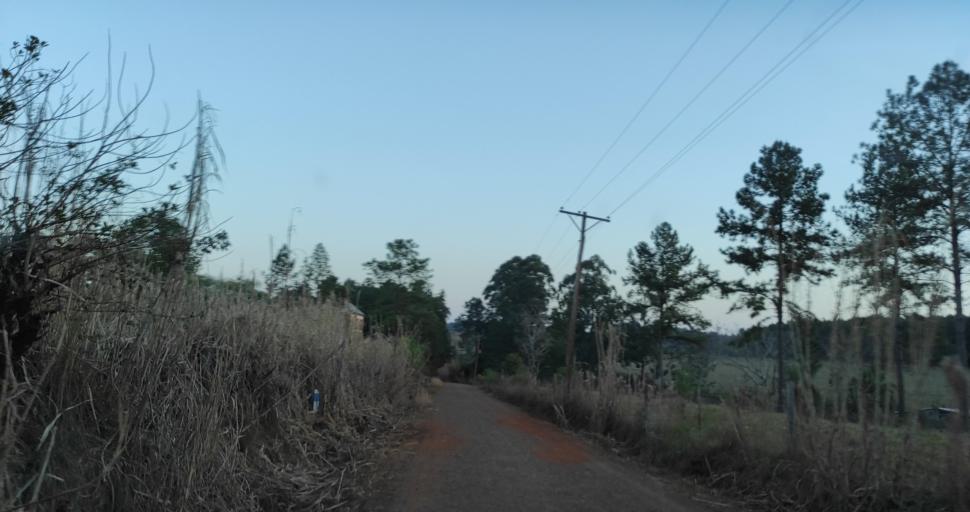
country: AR
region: Misiones
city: Capiovi
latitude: -26.8950
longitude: -55.0494
